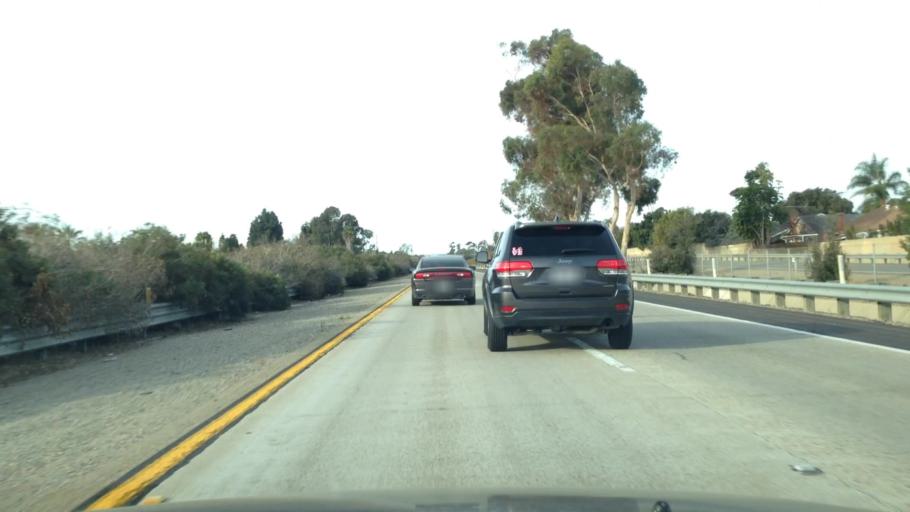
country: US
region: California
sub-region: Ventura County
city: Saticoy
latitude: 34.2760
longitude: -119.1824
